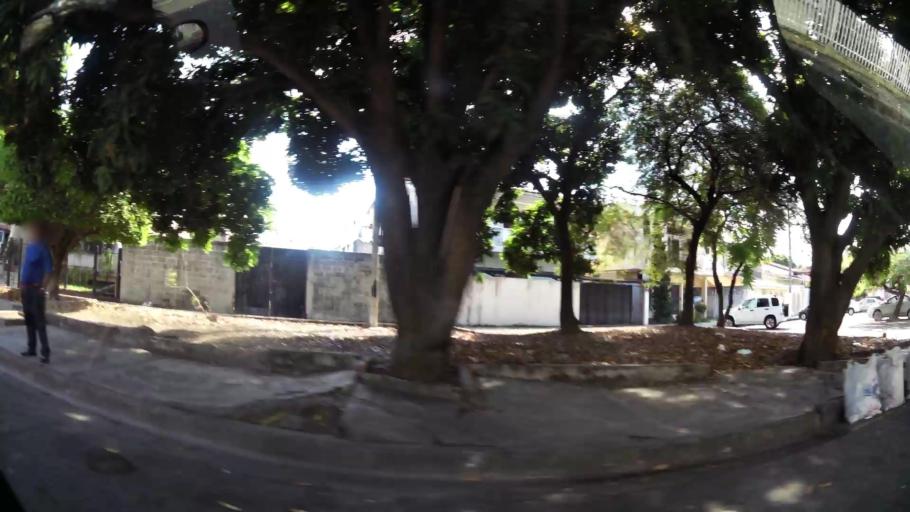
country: EC
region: Guayas
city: Guayaquil
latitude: -2.2249
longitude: -79.8968
